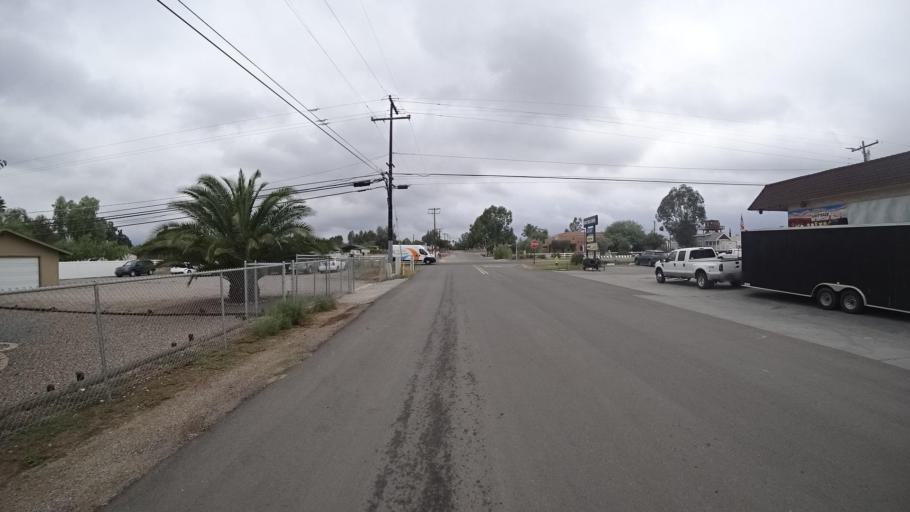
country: US
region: California
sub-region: San Diego County
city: Ramona
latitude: 33.0246
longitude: -116.8932
